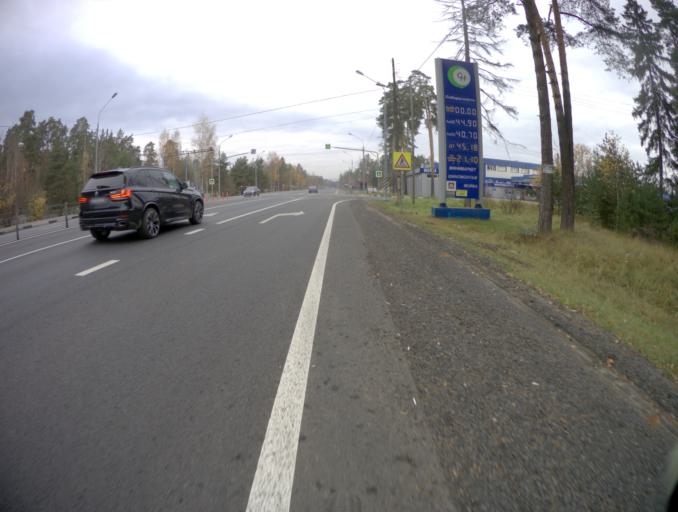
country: RU
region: Moskovskaya
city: Malaya Dubna
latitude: 55.8480
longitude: 38.9645
